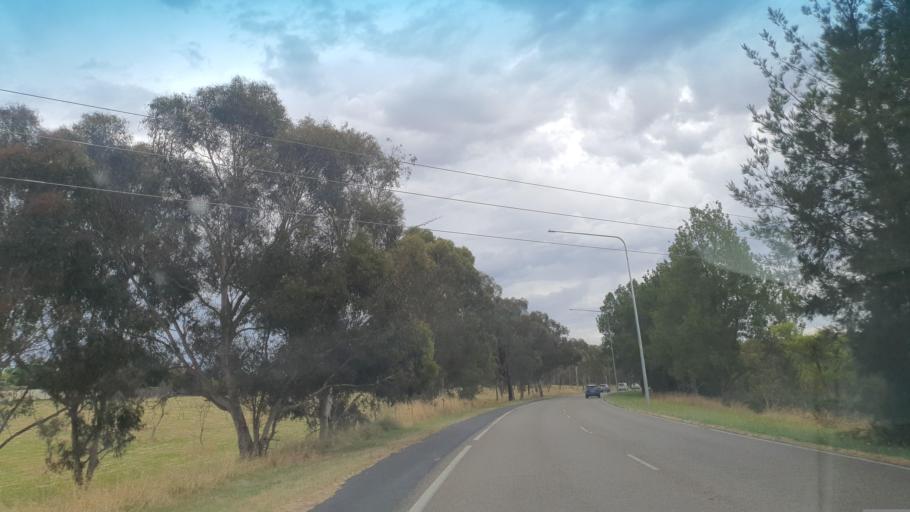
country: AU
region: Australian Capital Territory
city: Belconnen
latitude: -35.2137
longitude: 149.0381
